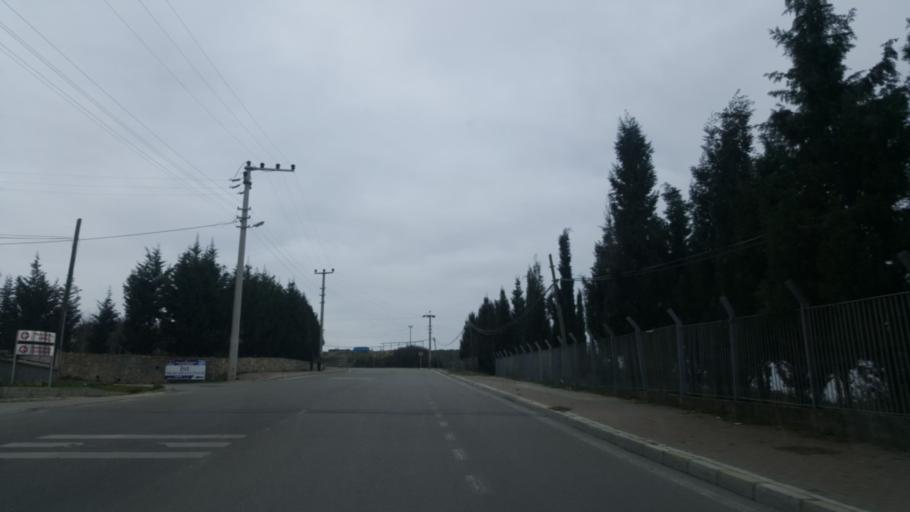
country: TR
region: Kocaeli
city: Tavsancil
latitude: 40.7965
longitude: 29.5523
